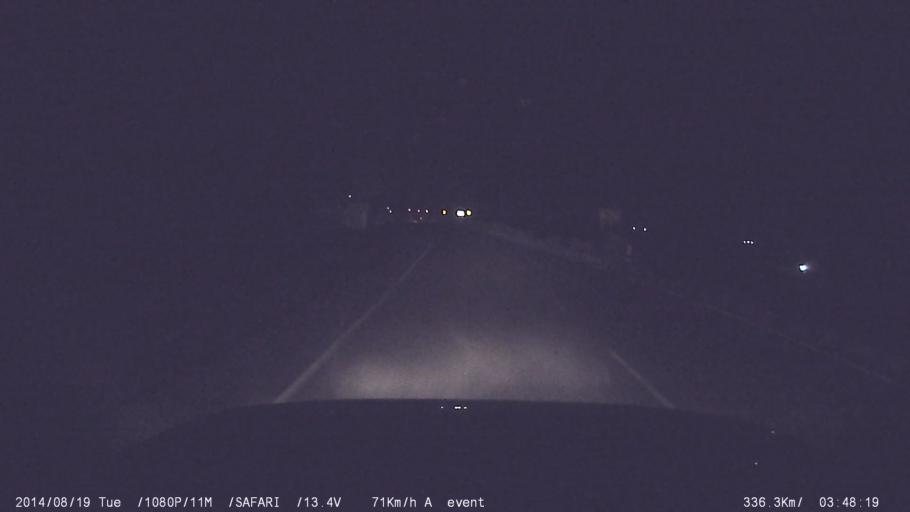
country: IN
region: Tamil Nadu
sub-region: Erode
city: Vijayapuri
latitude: 11.2372
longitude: 77.5065
